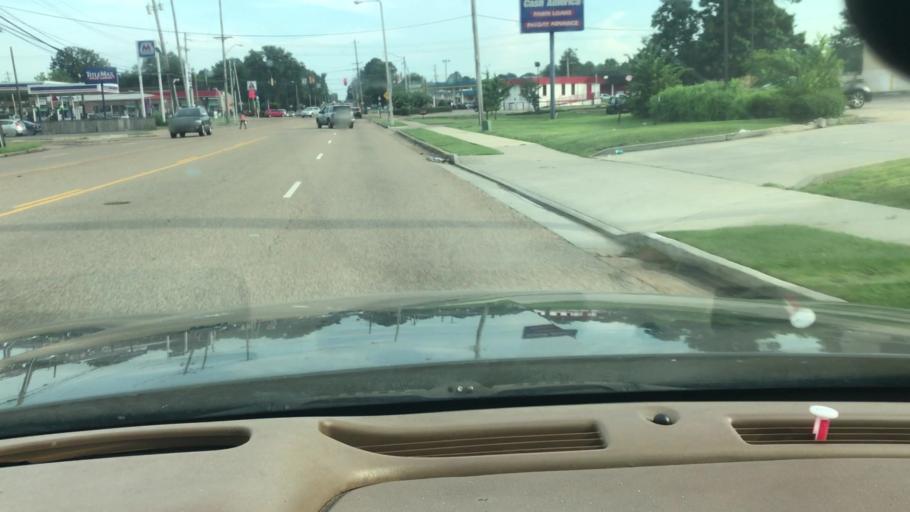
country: US
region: Tennessee
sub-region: Shelby County
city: New South Memphis
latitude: 35.0552
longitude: -90.0075
